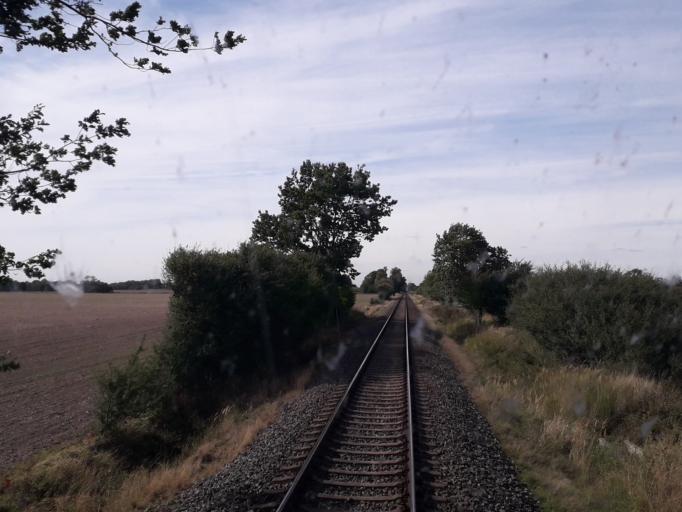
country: DE
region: Brandenburg
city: Neuruppin
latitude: 52.8664
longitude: 12.8775
